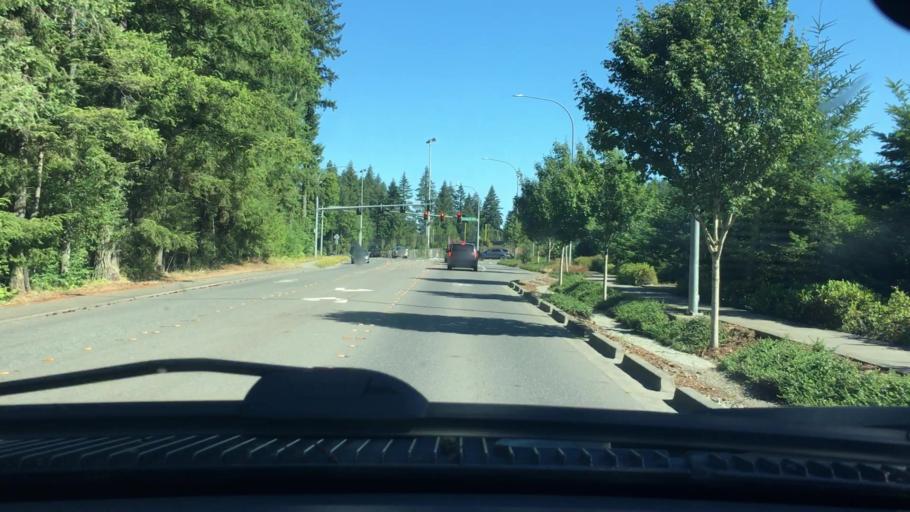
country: US
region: Washington
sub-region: King County
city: Issaquah
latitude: 47.5222
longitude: -122.0304
